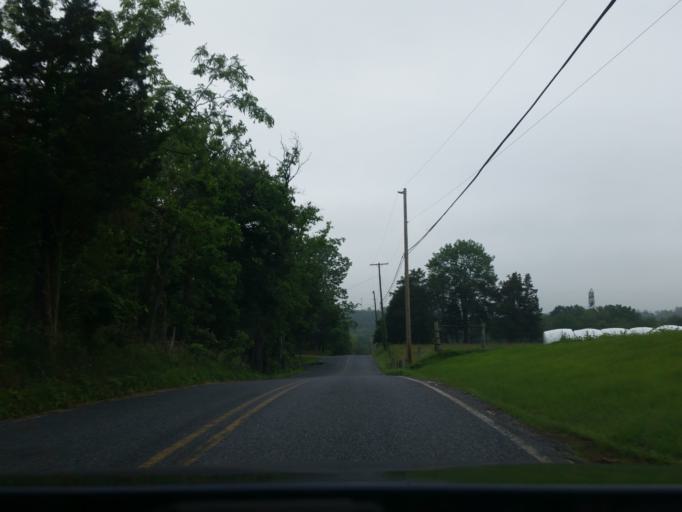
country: US
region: Pennsylvania
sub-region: Lebanon County
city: Jonestown
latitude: 40.4091
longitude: -76.5372
